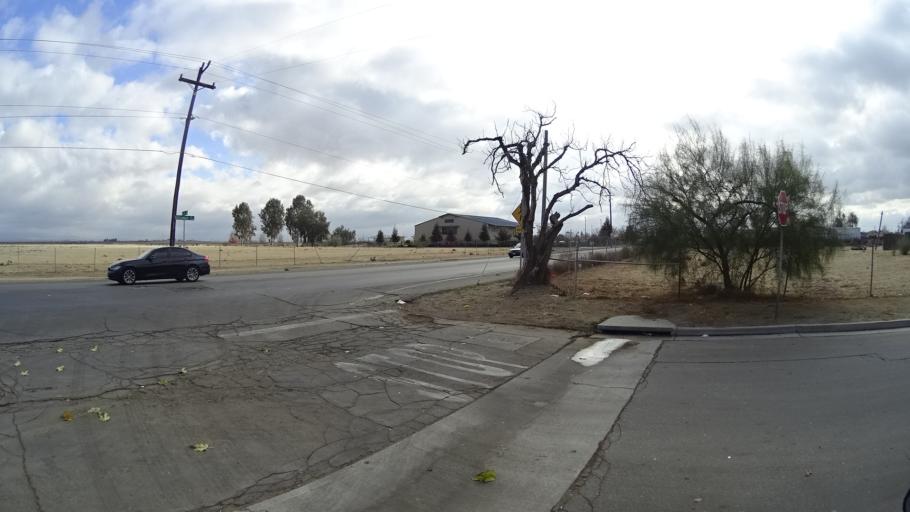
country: US
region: California
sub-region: Kern County
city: Bakersfield
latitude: 35.3296
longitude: -118.9856
